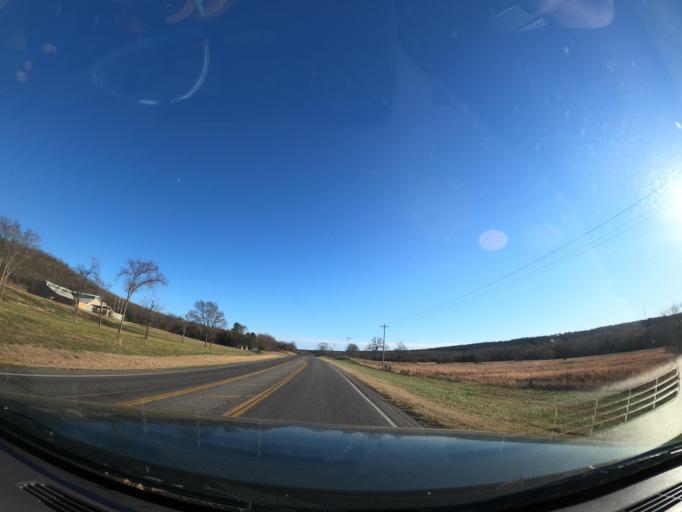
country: US
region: Oklahoma
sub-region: Latimer County
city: Wilburton
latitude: 34.9324
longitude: -95.3392
